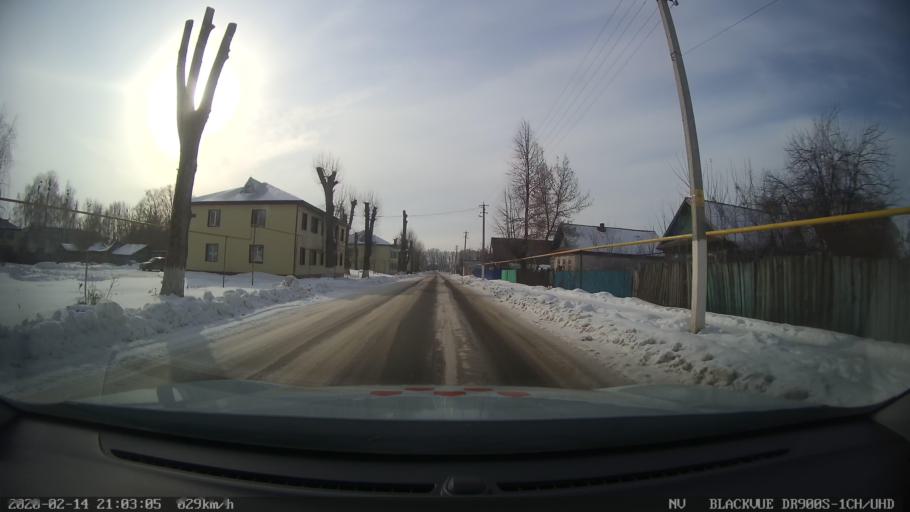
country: RU
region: Tatarstan
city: Kuybyshevskiy Zaton
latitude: 55.1580
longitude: 49.1768
